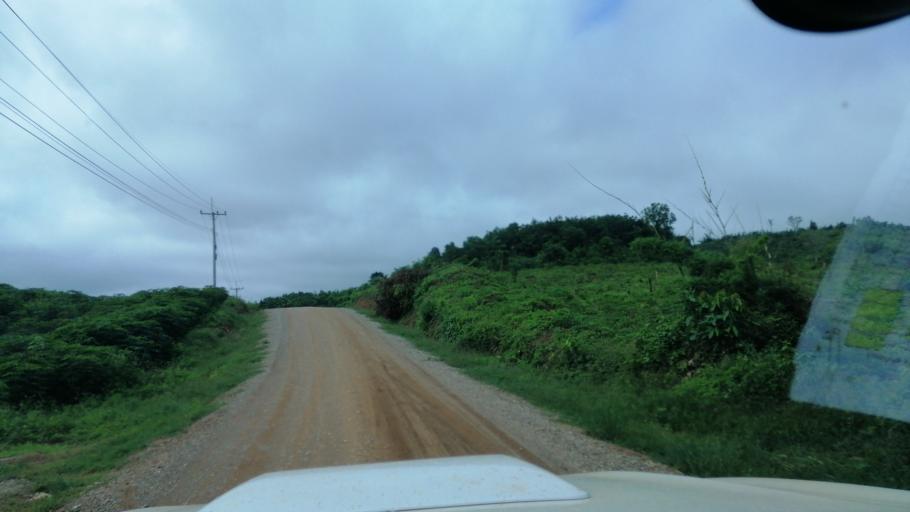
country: LA
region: Xiagnabouli
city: Muang Kenthao
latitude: 17.9829
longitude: 101.4159
